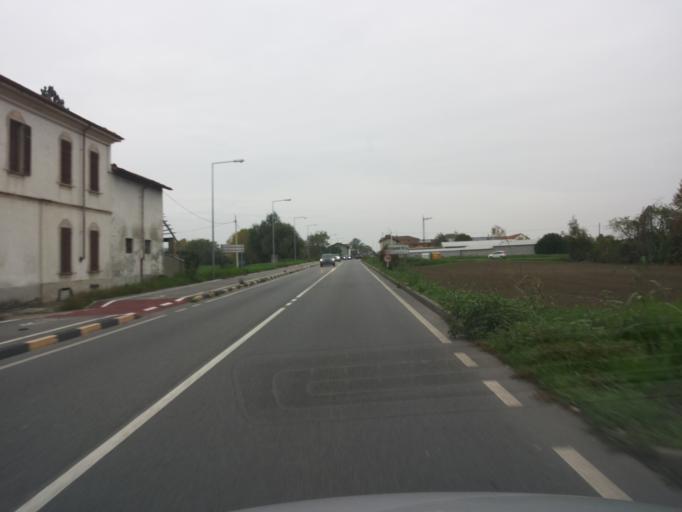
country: IT
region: Piedmont
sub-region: Provincia di Alessandria
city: Terruggia
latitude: 45.1052
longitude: 8.4521
